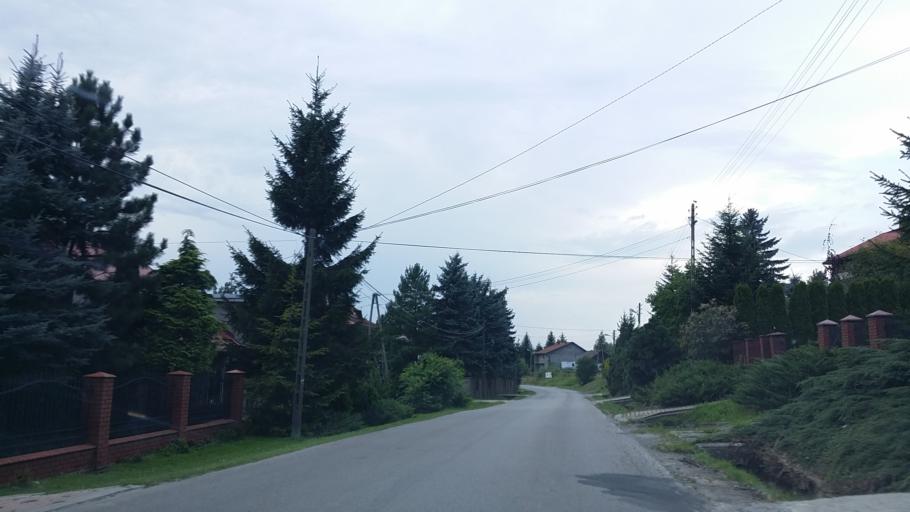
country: PL
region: Lesser Poland Voivodeship
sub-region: Powiat wielicki
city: Pawlikowice
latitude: 49.9749
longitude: 20.0204
